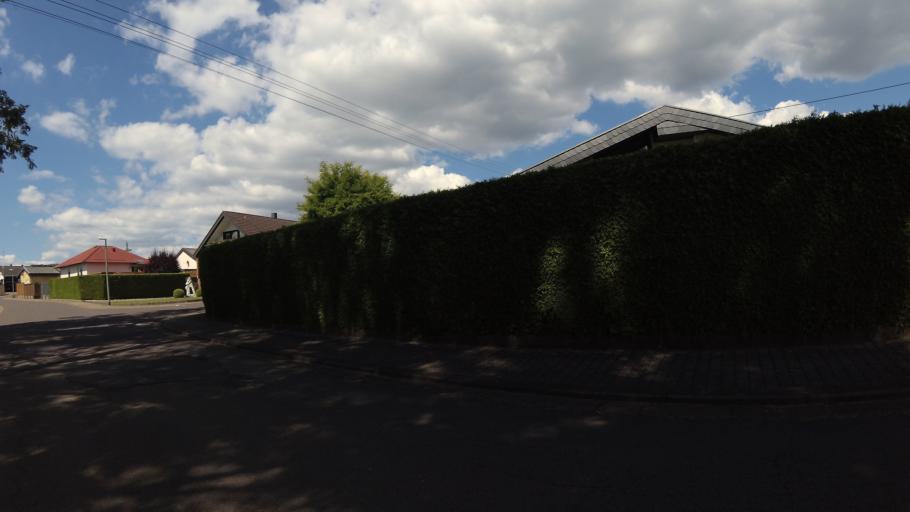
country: DE
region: Saarland
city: Weiskirchen
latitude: 49.5440
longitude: 6.7892
